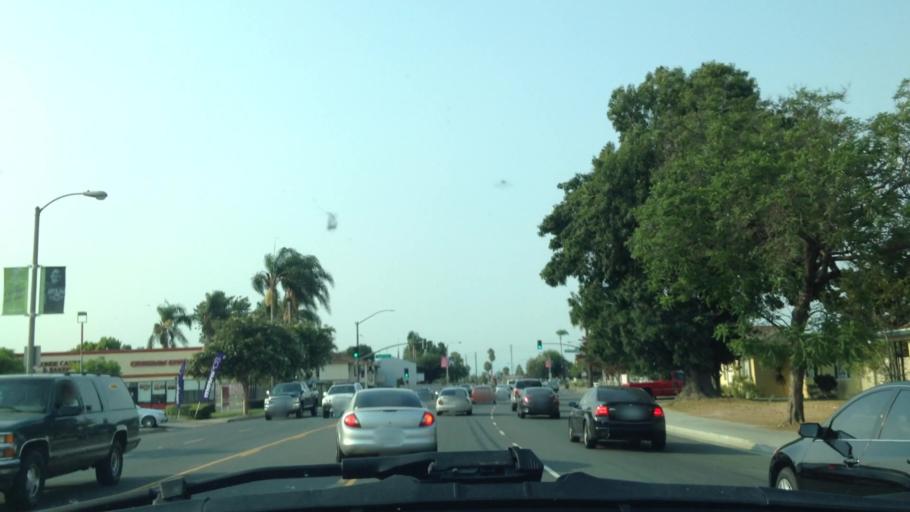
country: US
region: California
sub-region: Orange County
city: Santa Ana
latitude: 33.7624
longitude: -117.8518
